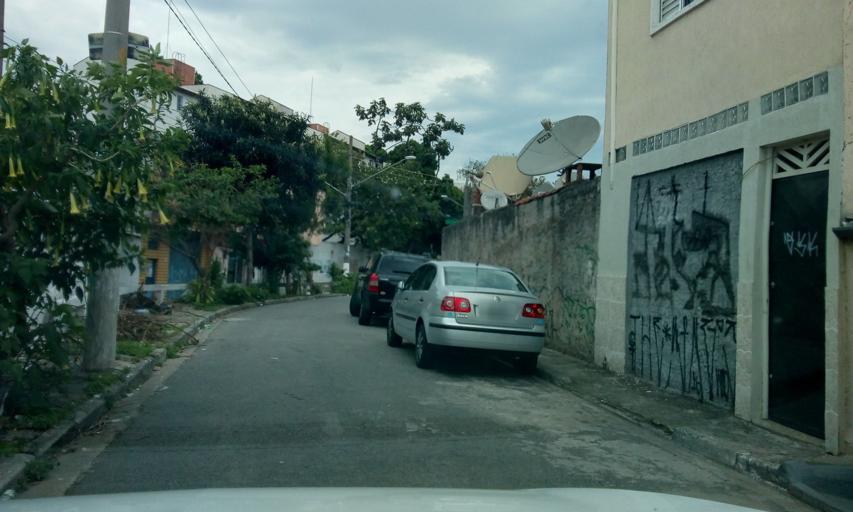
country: BR
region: Sao Paulo
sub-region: Sao Paulo
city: Sao Paulo
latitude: -23.5174
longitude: -46.7003
